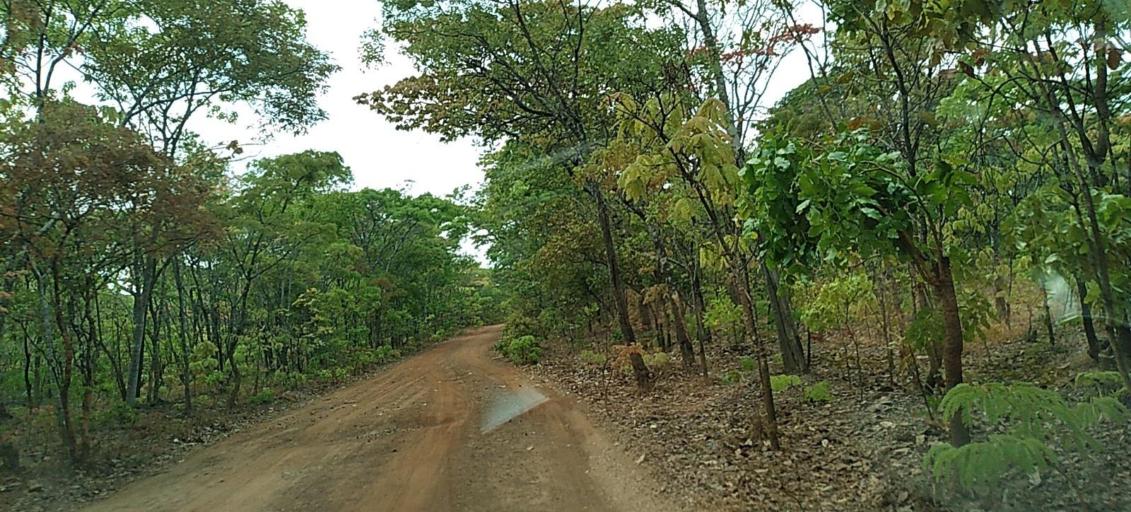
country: ZM
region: Copperbelt
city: Chililabombwe
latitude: -12.4957
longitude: 27.6387
